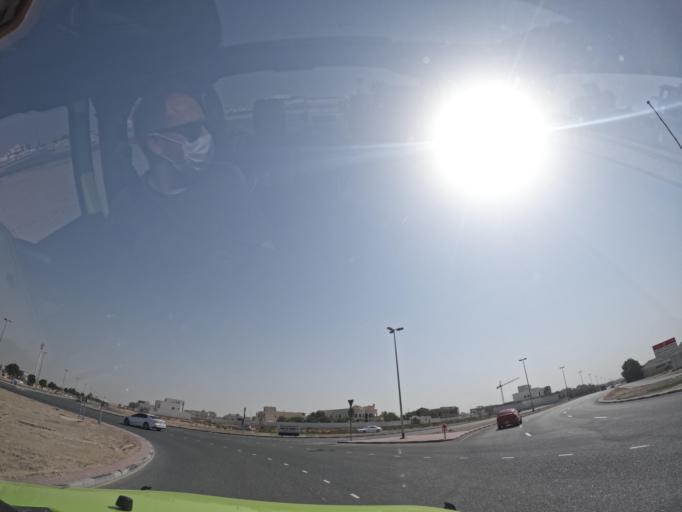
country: AE
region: Ash Shariqah
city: Sharjah
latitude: 25.1475
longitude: 55.3558
